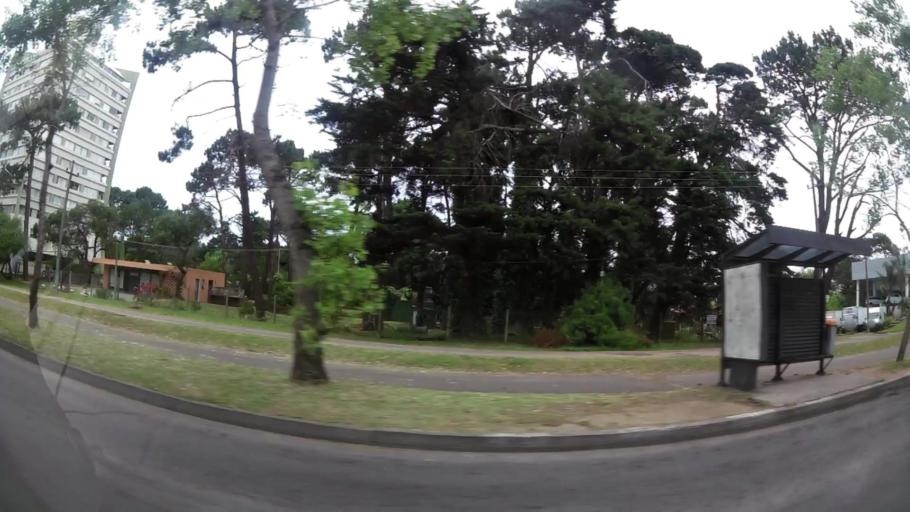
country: UY
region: Maldonado
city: Maldonado
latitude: -34.9312
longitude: -54.9431
